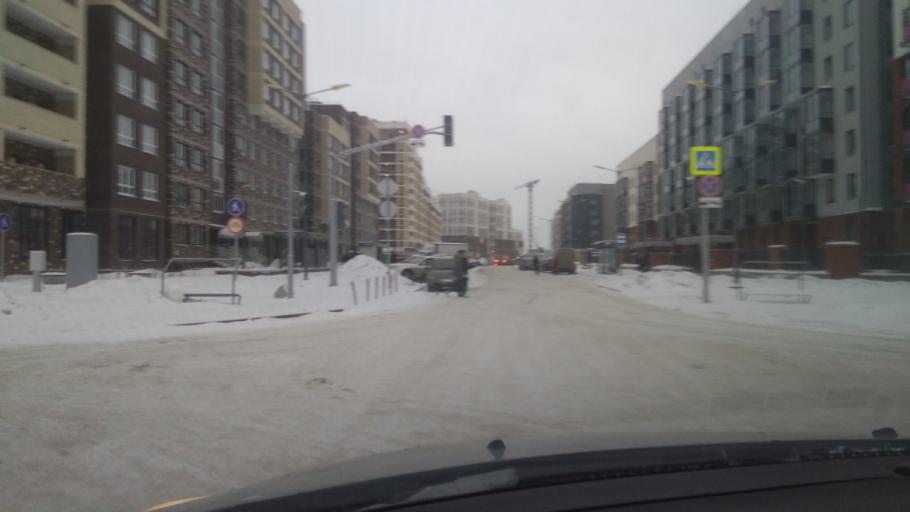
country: RU
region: Sverdlovsk
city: Sovkhoznyy
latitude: 56.7487
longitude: 60.5689
